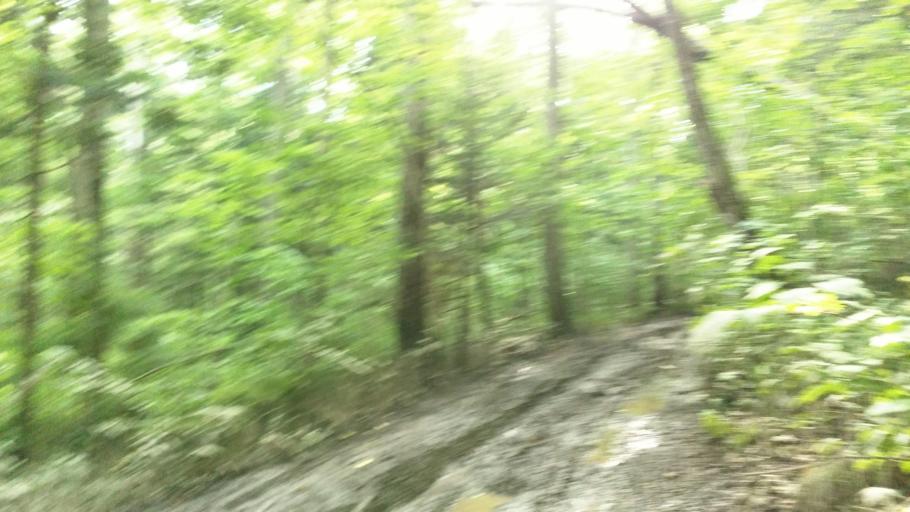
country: RU
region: Primorskiy
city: Trudovoye
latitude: 43.2065
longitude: 132.0084
